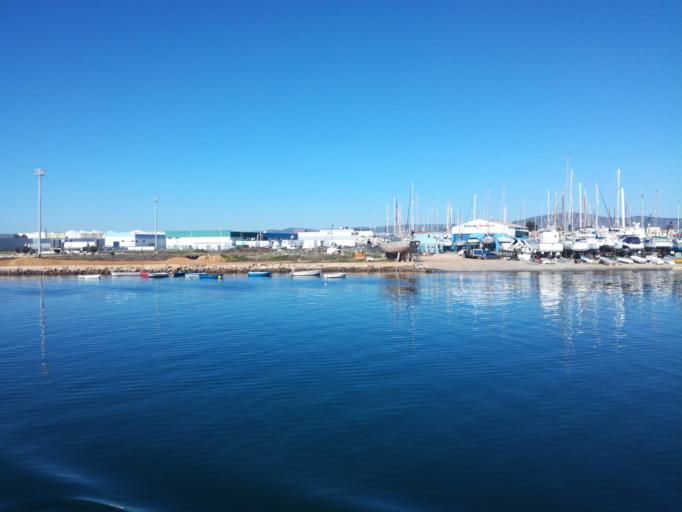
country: PT
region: Faro
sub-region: Olhao
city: Olhao
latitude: 37.0252
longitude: -7.8280
